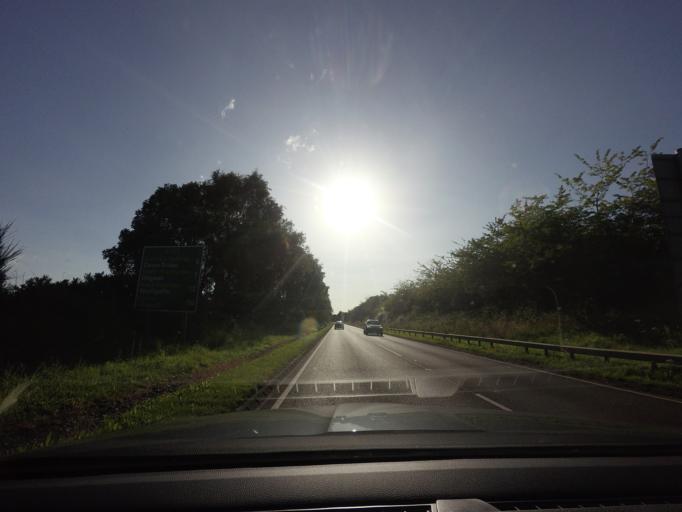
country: GB
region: Scotland
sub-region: Highland
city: Conon Bridge
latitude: 57.5405
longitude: -4.3395
